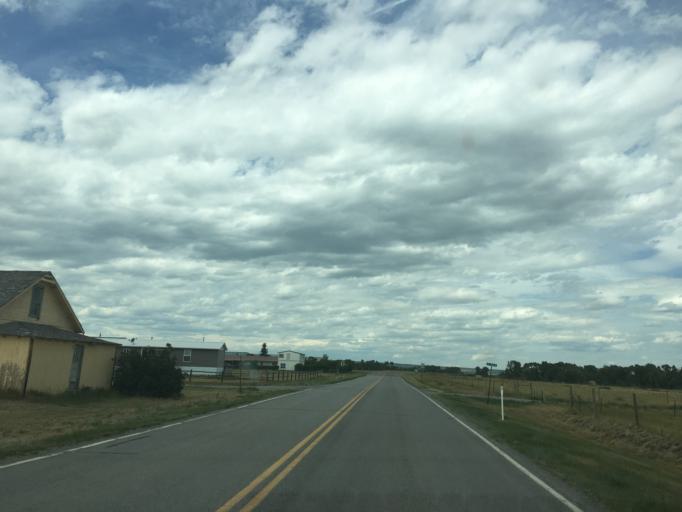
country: US
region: Montana
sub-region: Teton County
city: Choteau
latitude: 47.9792
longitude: -112.3128
